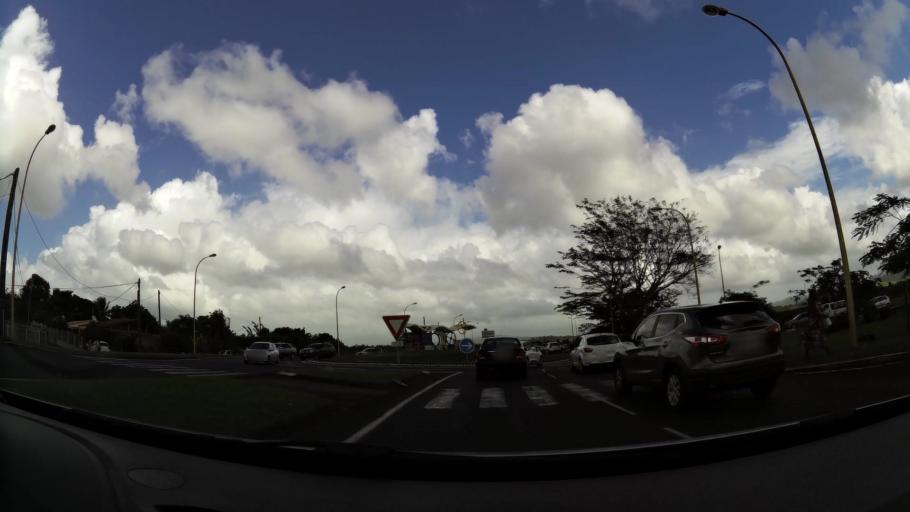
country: MQ
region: Martinique
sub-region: Martinique
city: Ducos
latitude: 14.5324
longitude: -60.9832
